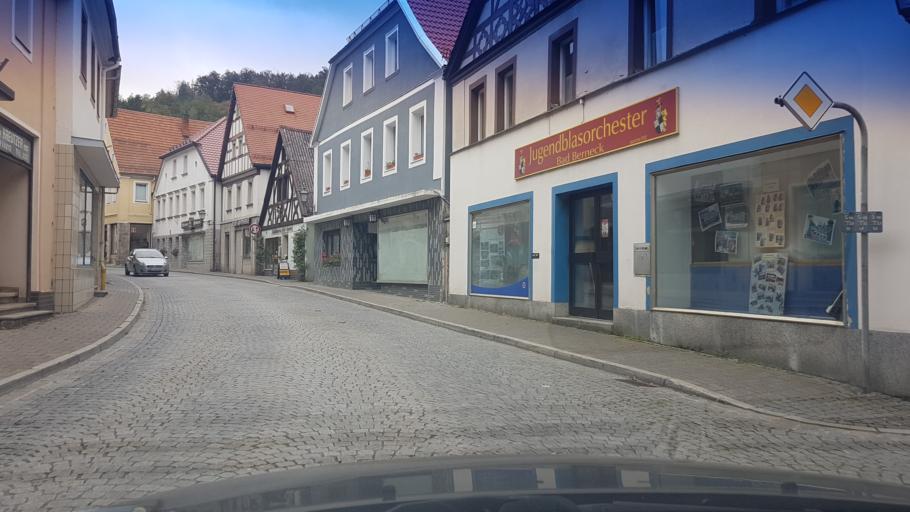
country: DE
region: Bavaria
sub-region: Upper Franconia
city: Bad Berneck im Fichtelgebirge
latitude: 50.0487
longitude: 11.6747
